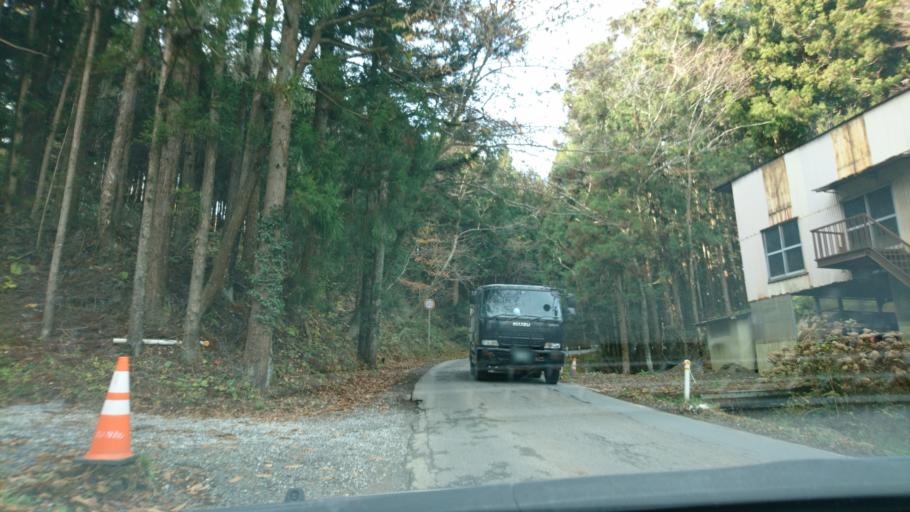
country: JP
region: Iwate
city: Ichinoseki
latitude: 39.0050
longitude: 141.2397
